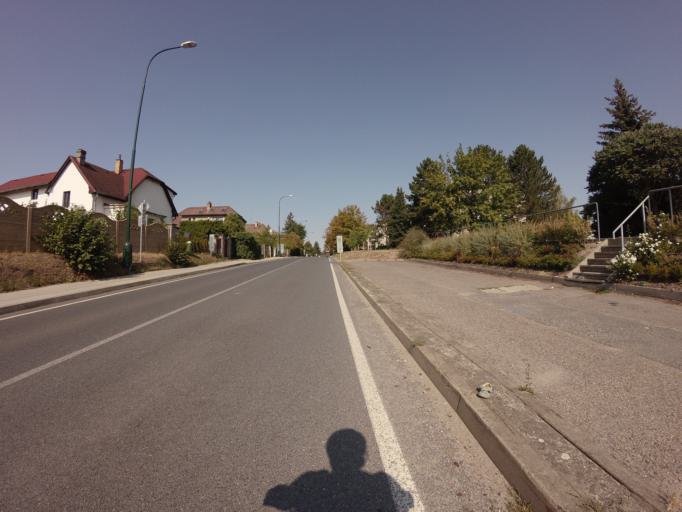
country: CZ
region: Central Bohemia
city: Tynec nad Sazavou
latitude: 49.8343
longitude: 14.5892
